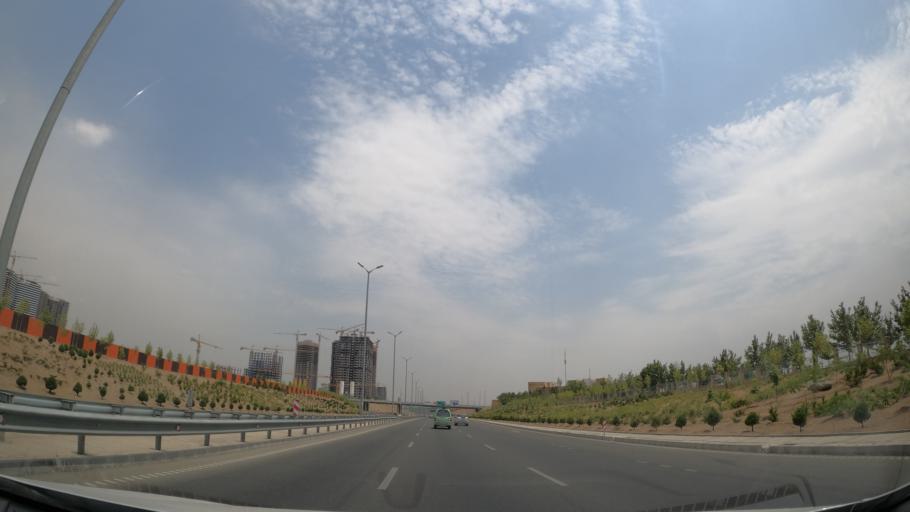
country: IR
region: Tehran
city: Shahr-e Qods
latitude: 35.7503
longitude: 51.1720
